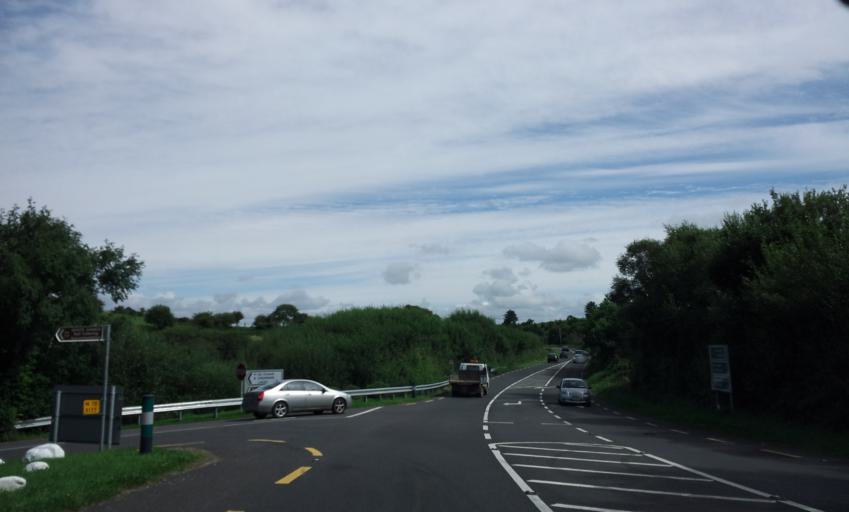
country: IE
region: Munster
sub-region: Ciarrai
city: Killorglin
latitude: 52.1037
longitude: -9.8214
